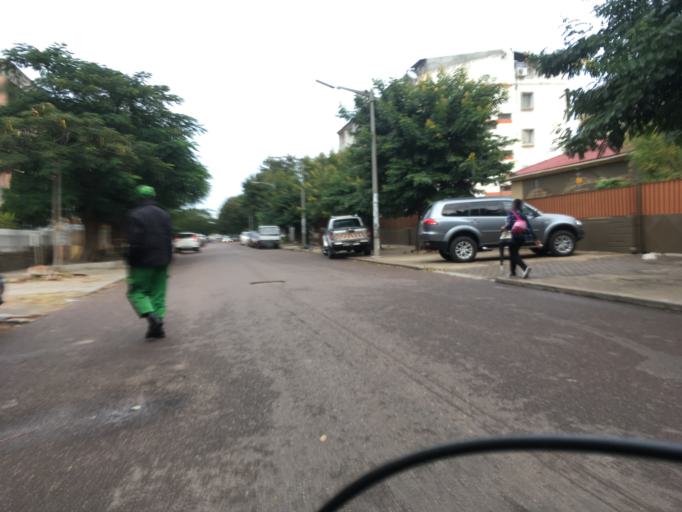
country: MZ
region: Maputo City
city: Maputo
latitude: -25.9633
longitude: 32.5915
